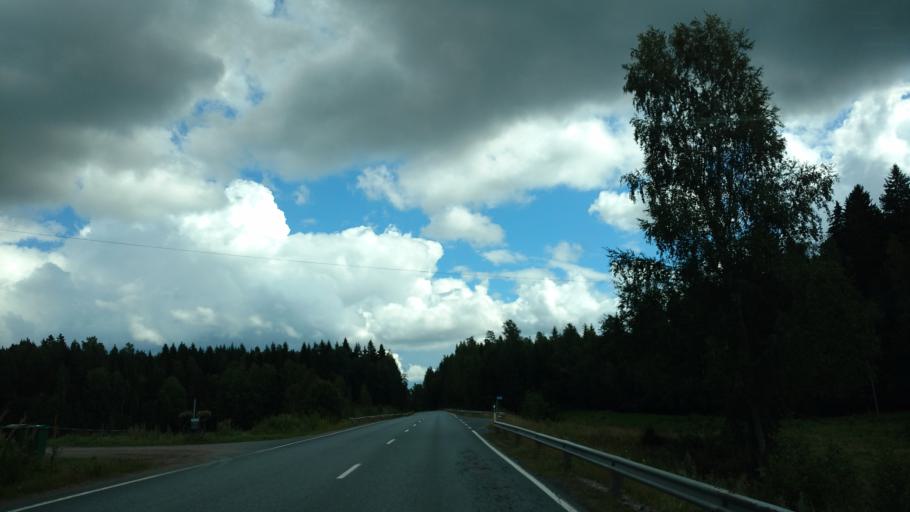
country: FI
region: Varsinais-Suomi
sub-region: Salo
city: Kisko
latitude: 60.2460
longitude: 23.5223
